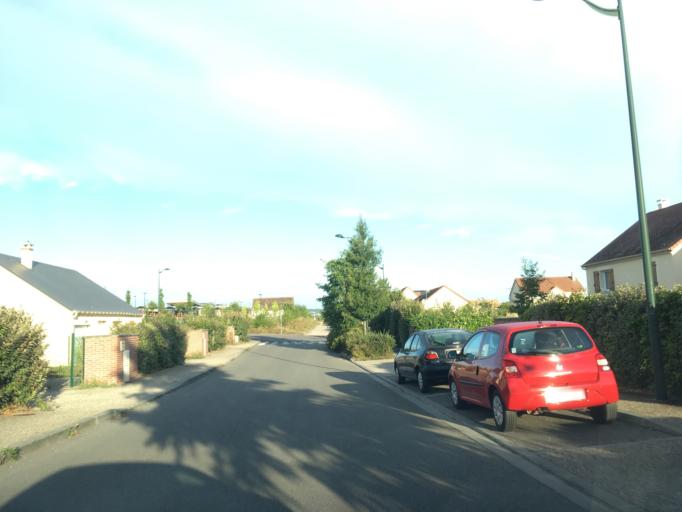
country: FR
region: Haute-Normandie
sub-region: Departement de l'Eure
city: Vernon
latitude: 49.0789
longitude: 1.4950
